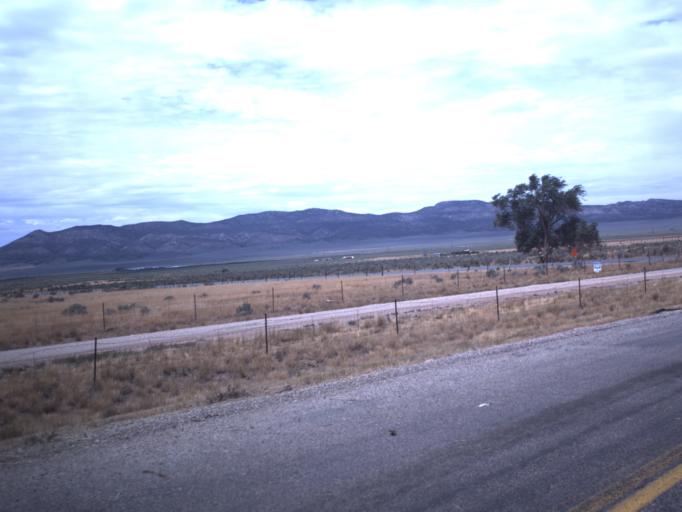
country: US
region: Utah
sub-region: Iron County
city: Parowan
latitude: 37.9109
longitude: -112.7793
